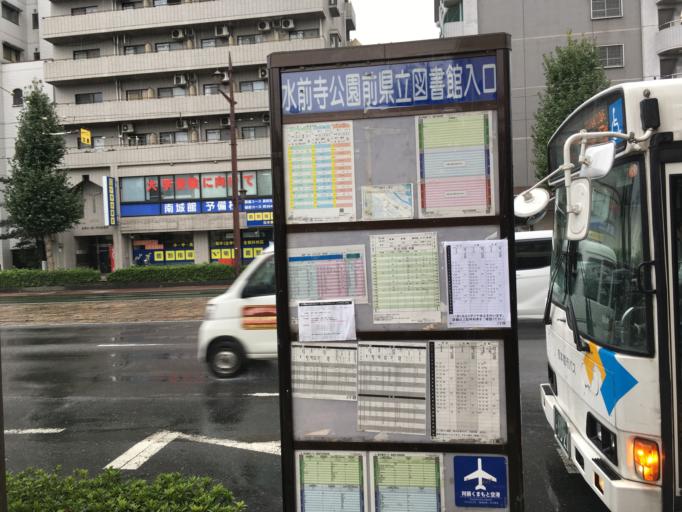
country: JP
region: Kumamoto
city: Kumamoto
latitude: 32.7893
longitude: 130.7334
